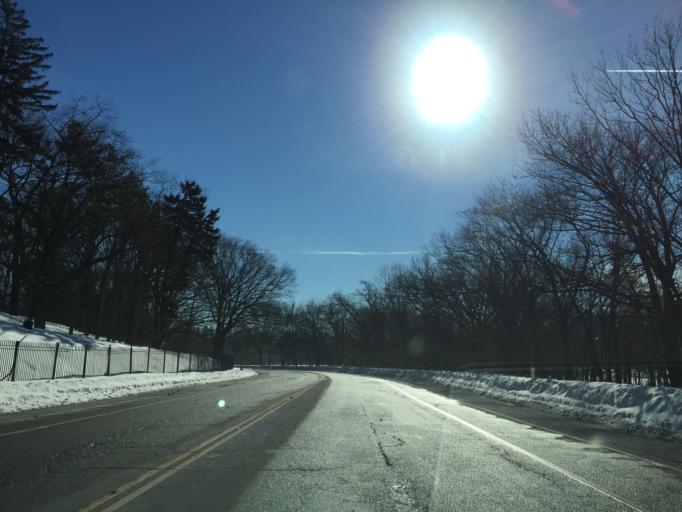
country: US
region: Massachusetts
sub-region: Middlesex County
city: Watertown
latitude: 42.3615
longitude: -71.1658
